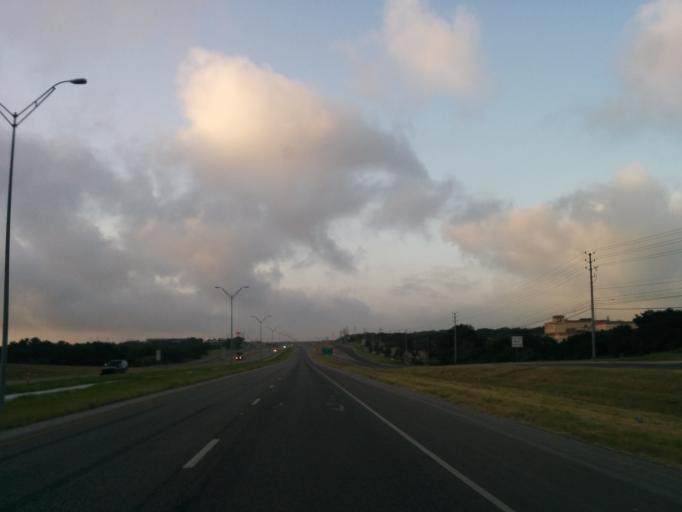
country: US
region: Texas
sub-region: Bexar County
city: Leon Valley
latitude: 29.4704
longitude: -98.6959
